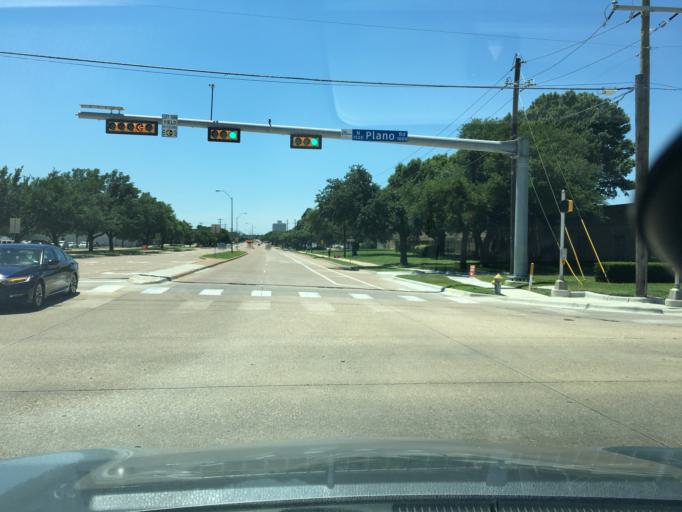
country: US
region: Texas
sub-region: Dallas County
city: Richardson
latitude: 32.9680
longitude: -96.6999
